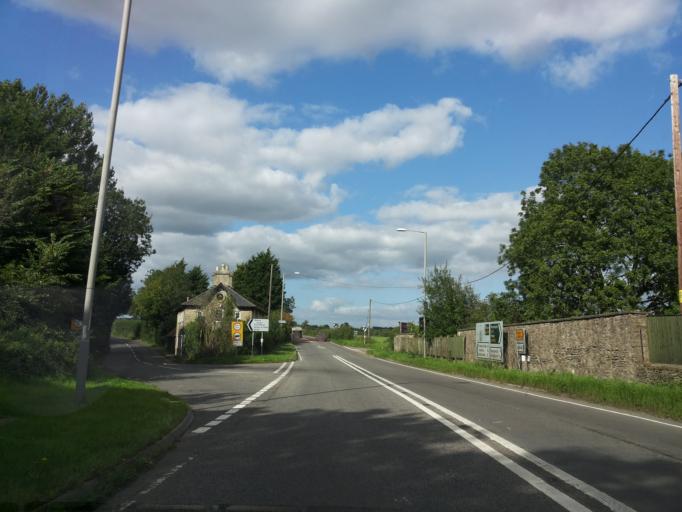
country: GB
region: England
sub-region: Bath and North East Somerset
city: Hinton Charterhouse
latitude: 51.2858
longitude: -2.3001
